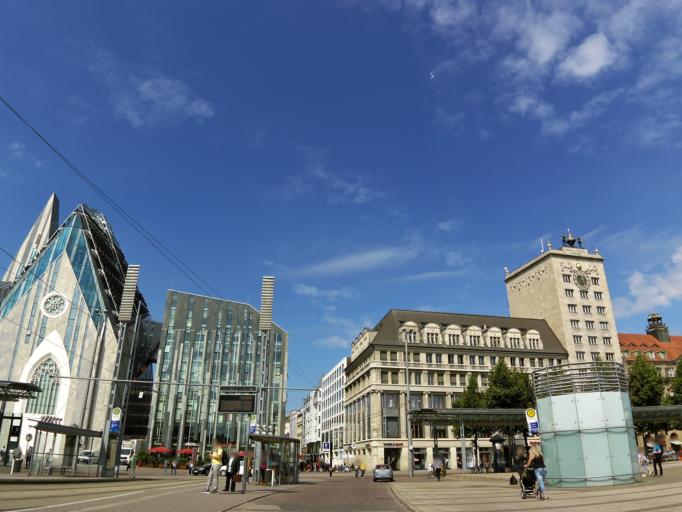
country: DE
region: Saxony
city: Leipzig
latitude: 51.3391
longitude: 12.3810
